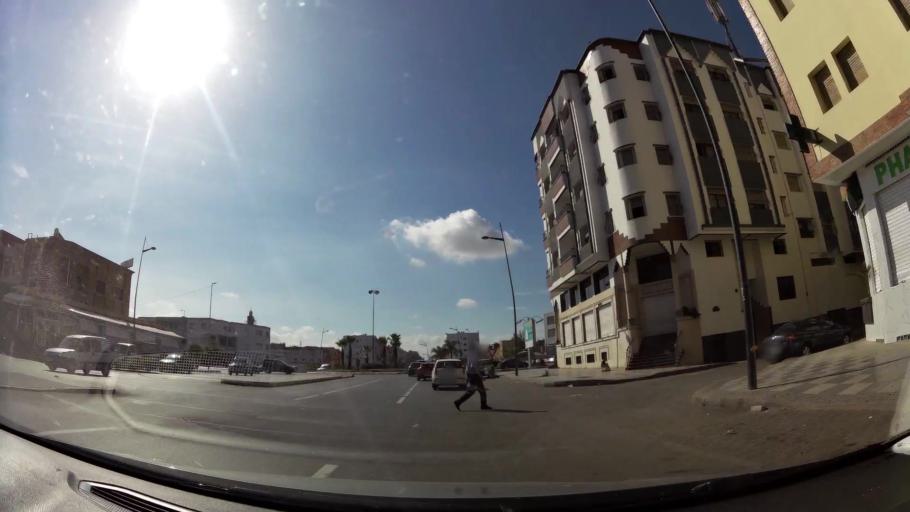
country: MA
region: Rabat-Sale-Zemmour-Zaer
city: Sale
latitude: 34.0691
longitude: -6.7921
